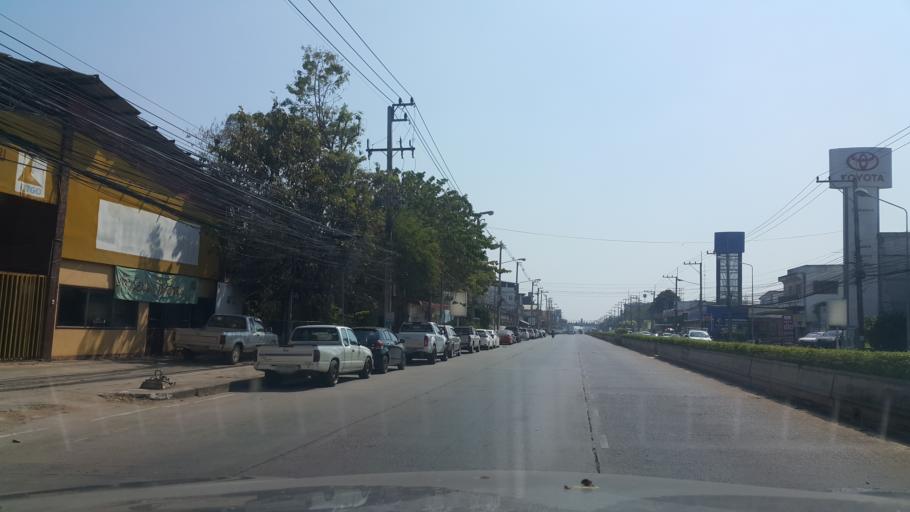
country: TH
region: Changwat Udon Thani
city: Udon Thani
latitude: 17.3906
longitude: 102.8002
